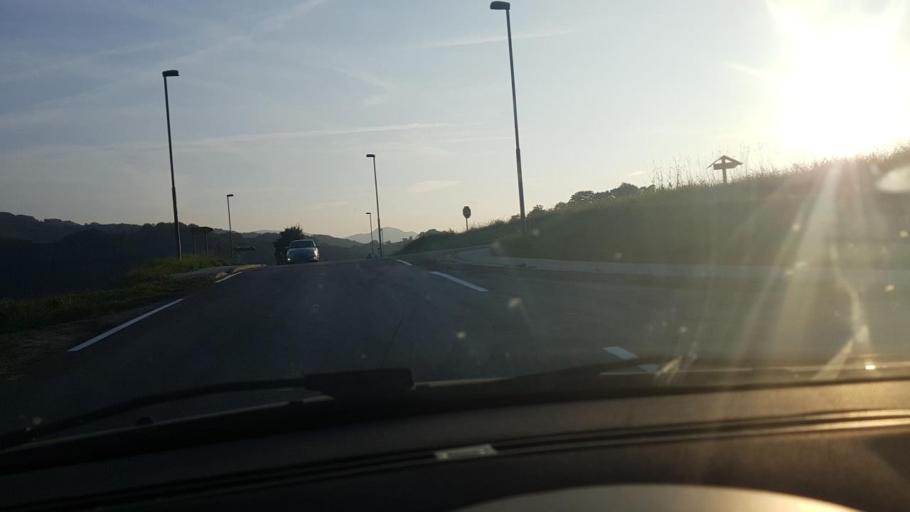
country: SI
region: Majsperk
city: Majsperk
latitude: 46.3356
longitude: 15.7004
